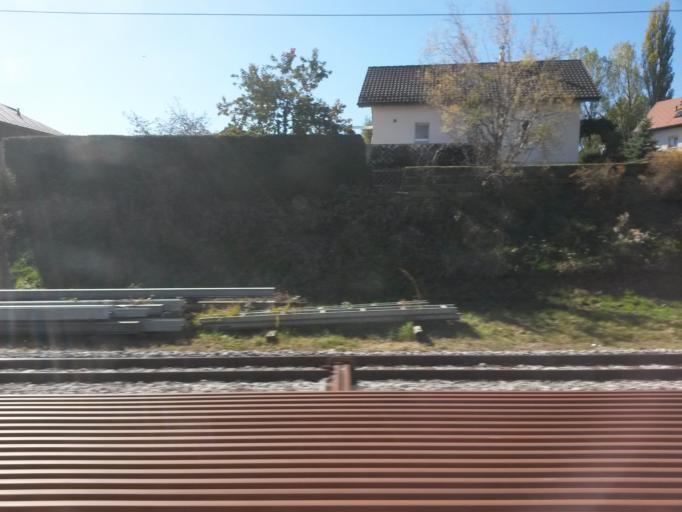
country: CH
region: Fribourg
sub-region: Gruyere District
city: Bulle
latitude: 46.6209
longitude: 7.0493
